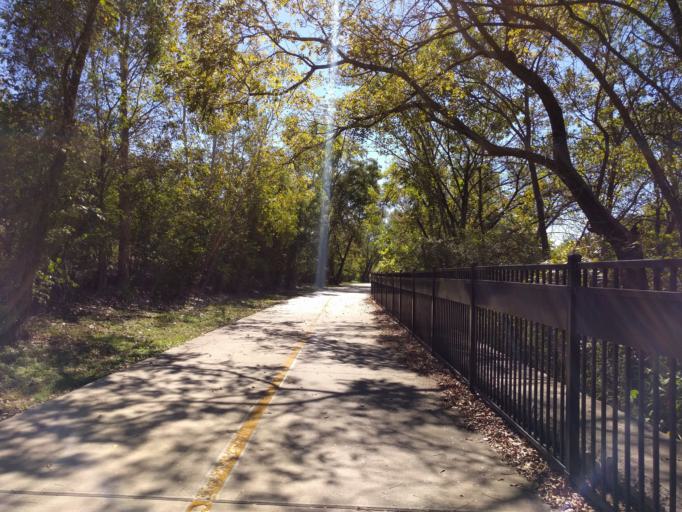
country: US
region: Texas
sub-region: Dallas County
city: Richardson
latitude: 32.9066
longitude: -96.7634
